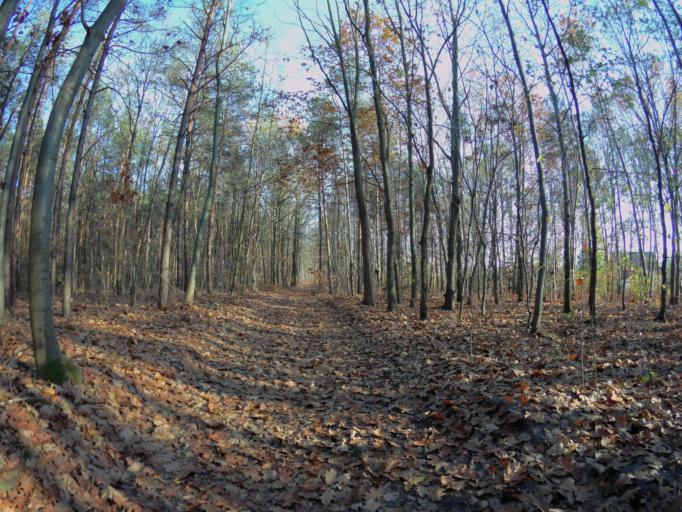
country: PL
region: Subcarpathian Voivodeship
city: Nowa Sarzyna
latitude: 50.3046
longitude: 22.3586
